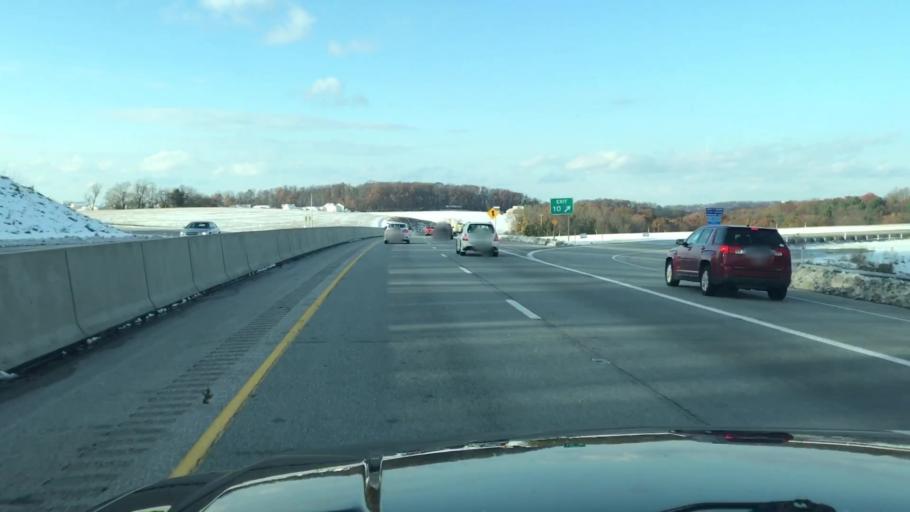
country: US
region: Pennsylvania
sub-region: York County
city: Loganville
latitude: 39.8664
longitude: -76.6983
